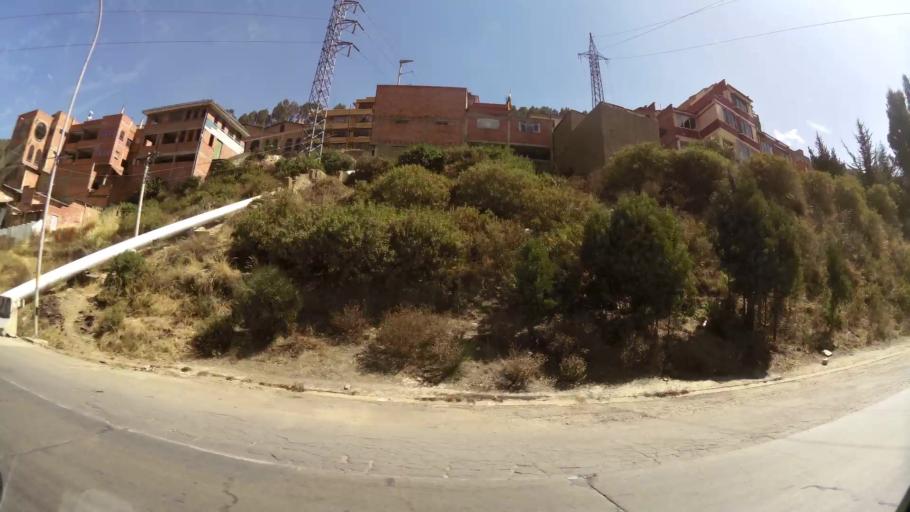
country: BO
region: La Paz
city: La Paz
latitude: -16.4654
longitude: -68.1526
